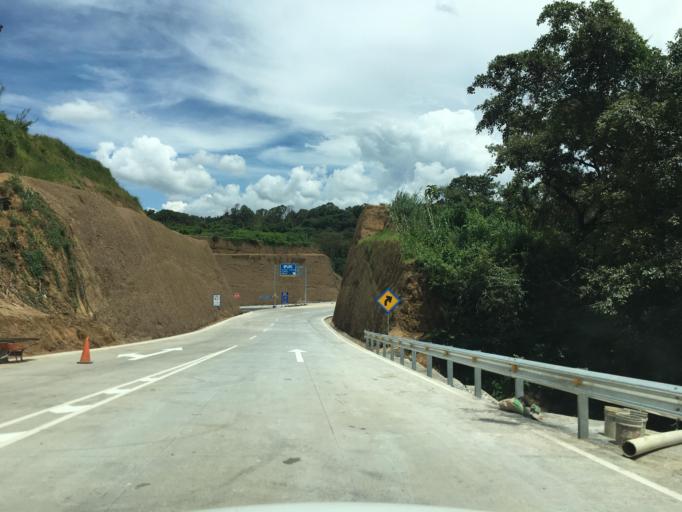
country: GT
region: Guatemala
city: Santa Catarina Pinula
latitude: 14.5746
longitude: -90.5405
